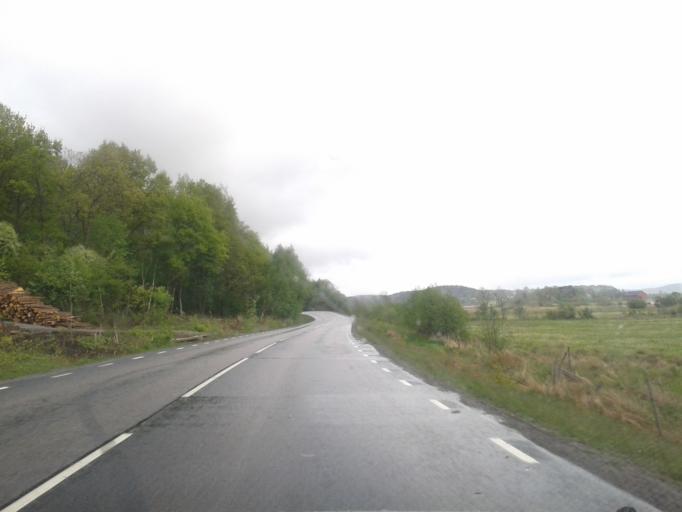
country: SE
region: Vaestra Goetaland
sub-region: Ale Kommun
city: Alvangen
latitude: 57.9603
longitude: 12.0955
